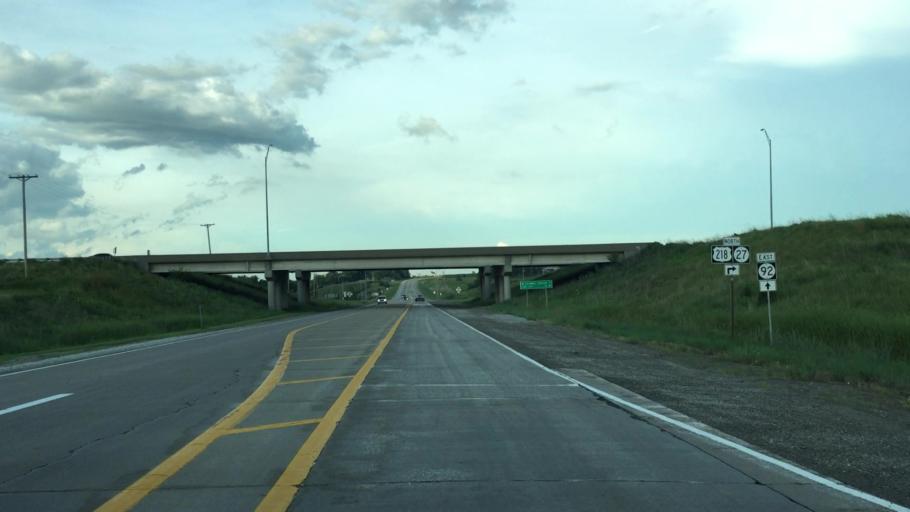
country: US
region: Iowa
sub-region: Washington County
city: Washington
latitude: 41.2909
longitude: -91.5354
